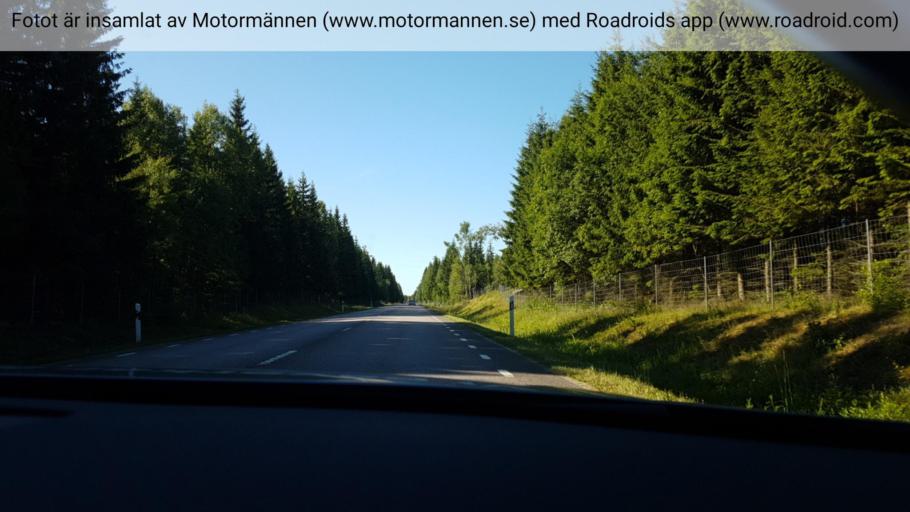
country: SE
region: Vaestra Goetaland
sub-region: Falkopings Kommun
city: Falkoeping
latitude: 58.0425
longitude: 13.5479
